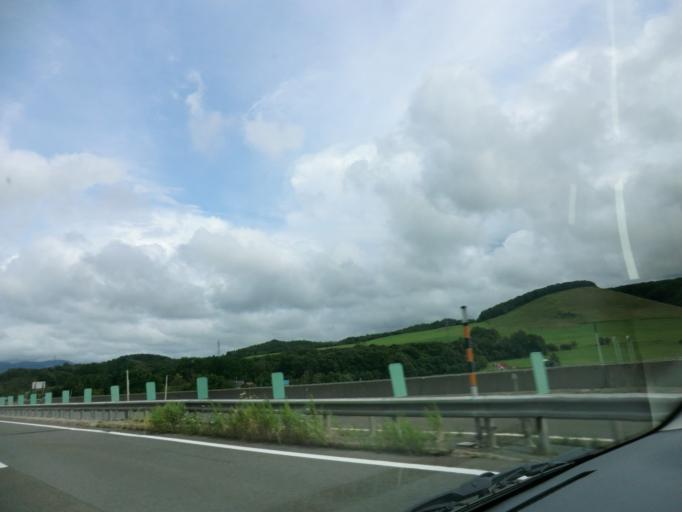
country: JP
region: Hokkaido
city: Iwamizawa
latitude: 43.2167
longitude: 141.8237
